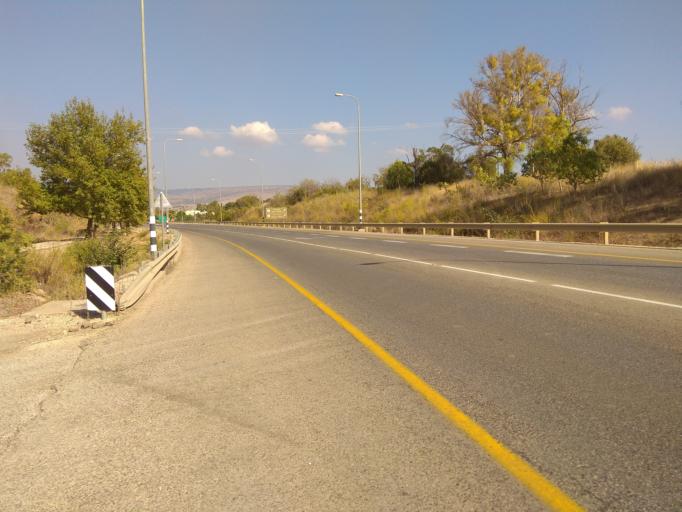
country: IL
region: Northern District
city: Qiryat Shemona
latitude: 33.2238
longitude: 35.6179
